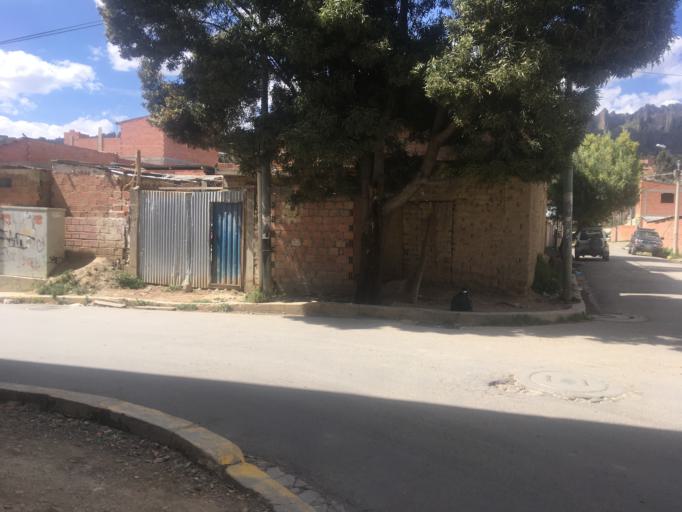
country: BO
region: La Paz
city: La Paz
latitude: -16.5402
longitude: -68.0446
